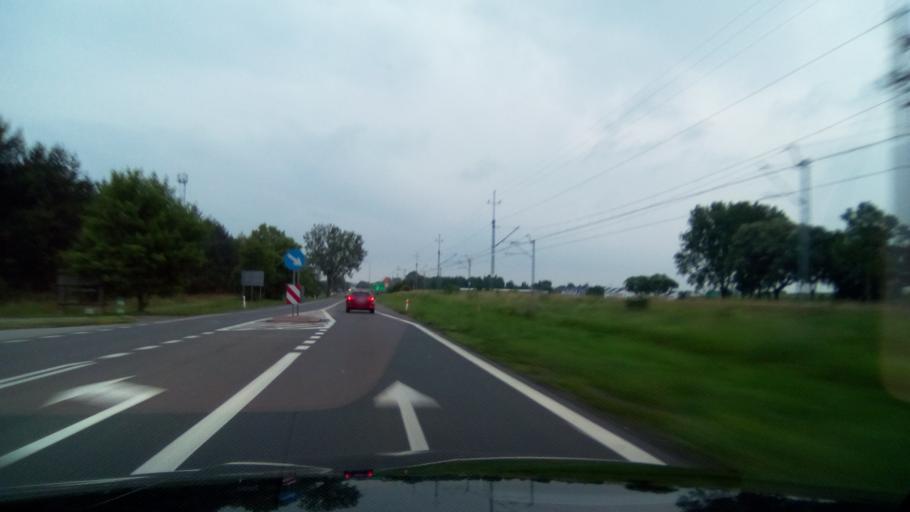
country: PL
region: Greater Poland Voivodeship
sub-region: Powiat poznanski
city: Pobiedziska
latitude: 52.4754
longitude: 17.2489
